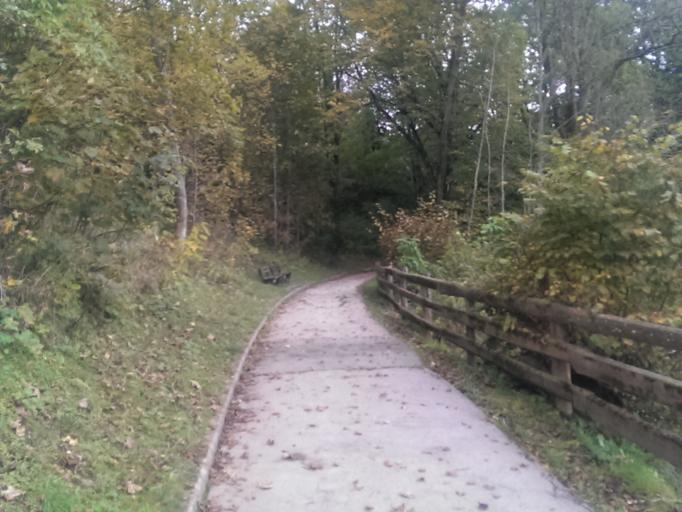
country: AT
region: Styria
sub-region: Politischer Bezirk Bruck-Muerzzuschlag
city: Mariazell
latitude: 47.7775
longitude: 15.3123
